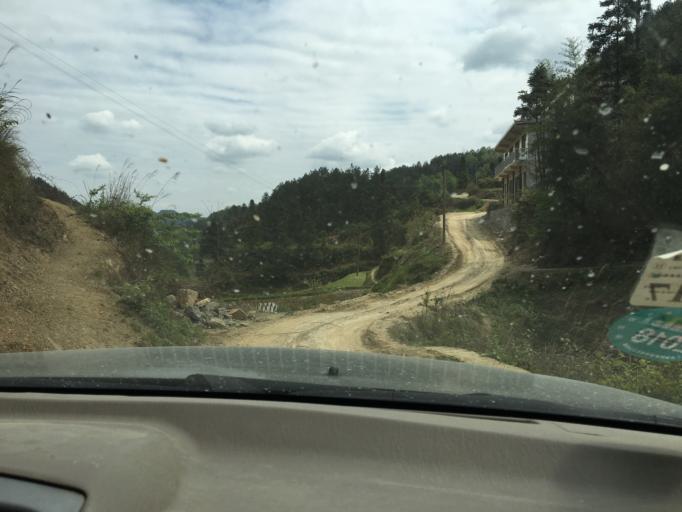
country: CN
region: Guizhou Sheng
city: Kuanping
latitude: 28.0216
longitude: 108.0592
